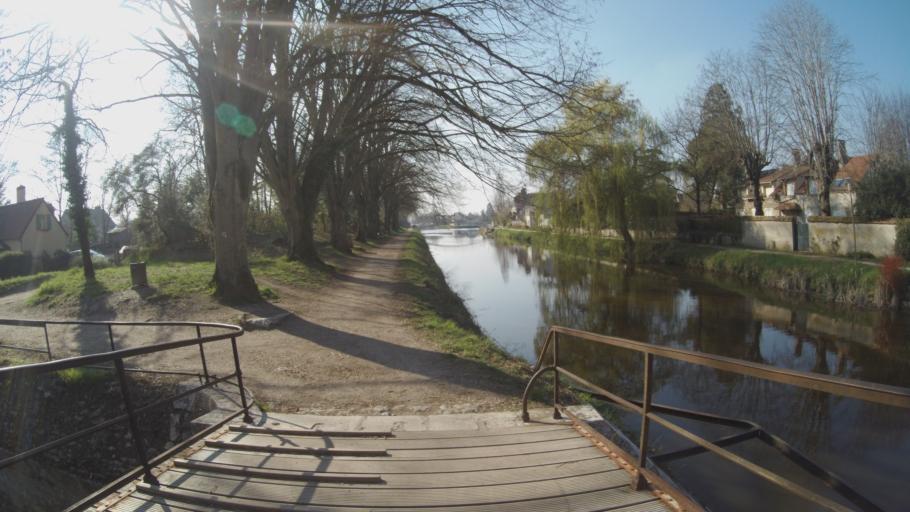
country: FR
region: Centre
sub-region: Departement du Loiret
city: Saint-Jean-de-Braye
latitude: 47.8980
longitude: 1.9912
